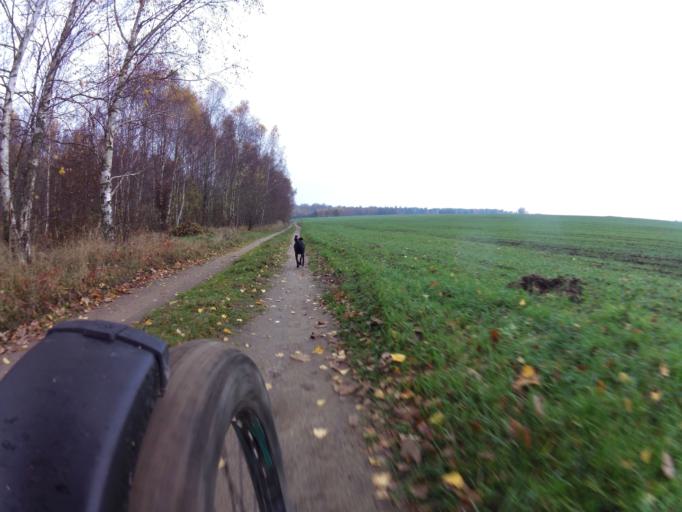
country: PL
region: Pomeranian Voivodeship
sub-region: Powiat pucki
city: Krokowa
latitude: 54.7247
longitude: 18.1324
